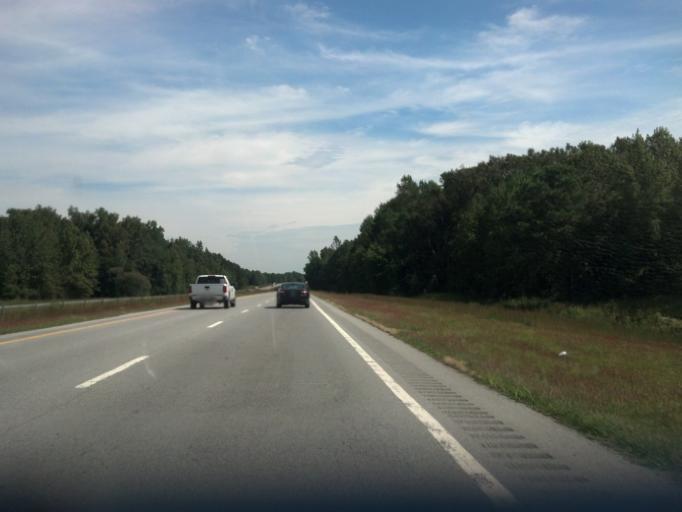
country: US
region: North Carolina
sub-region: Pitt County
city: Farmville
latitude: 35.6050
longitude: -77.5204
